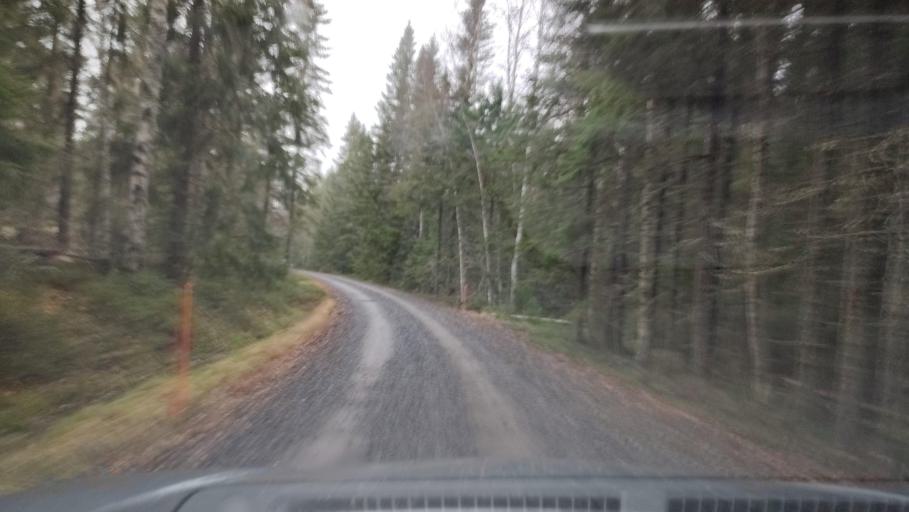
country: FI
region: Southern Ostrobothnia
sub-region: Suupohja
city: Karijoki
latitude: 62.1392
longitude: 21.6274
